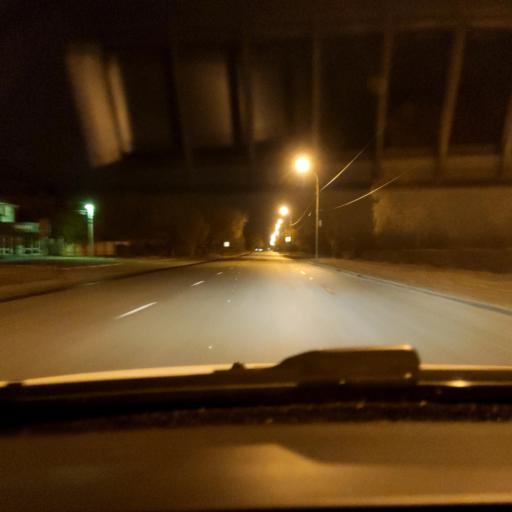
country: RU
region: Voronezj
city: Voronezh
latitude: 51.6402
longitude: 39.2108
